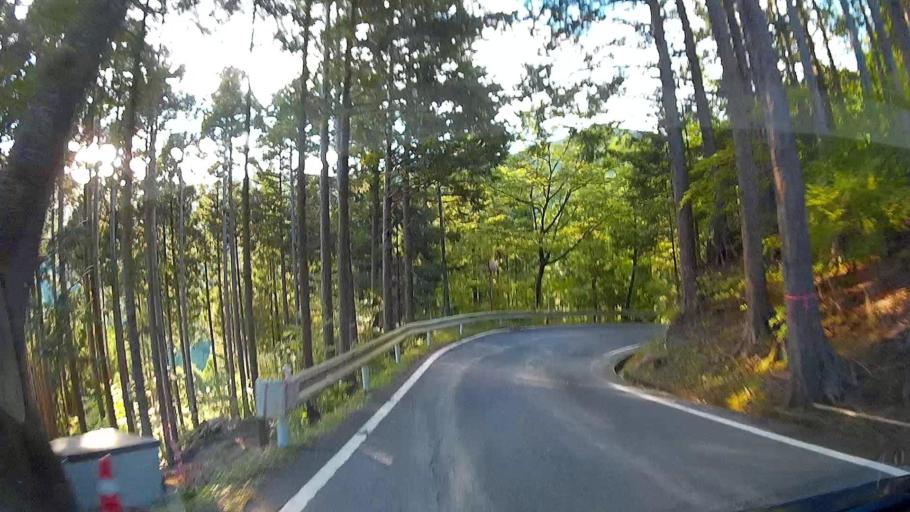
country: JP
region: Shizuoka
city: Shizuoka-shi
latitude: 35.1582
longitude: 138.2613
